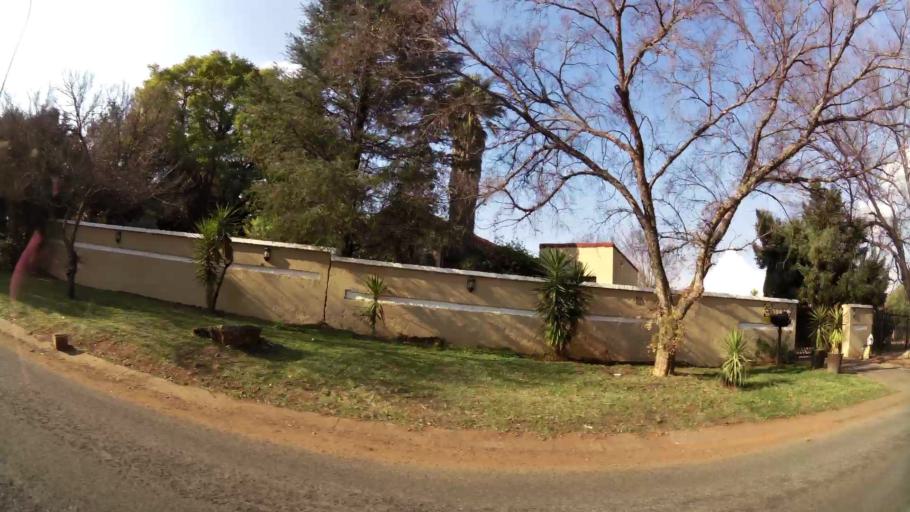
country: ZA
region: Gauteng
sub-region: Ekurhuleni Metropolitan Municipality
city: Tembisa
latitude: -25.9570
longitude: 28.2182
